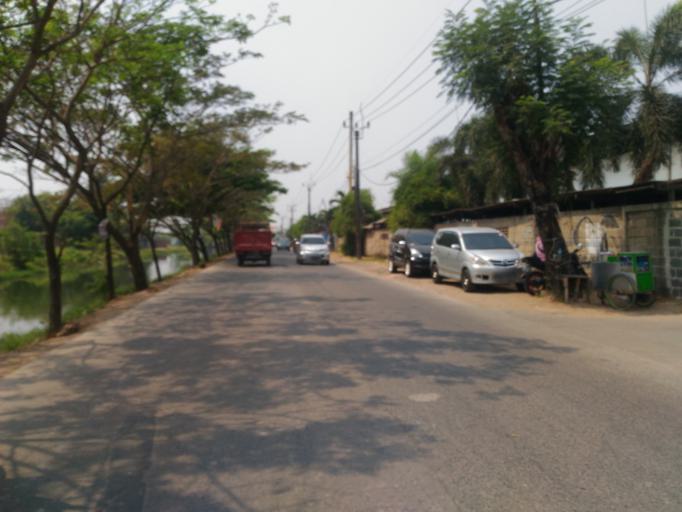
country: ID
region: West Java
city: Sepatan
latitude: -6.1475
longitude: 106.5753
